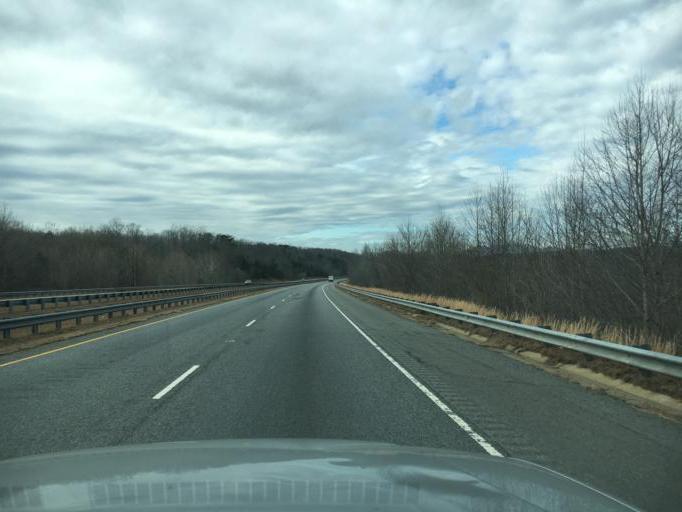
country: US
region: North Carolina
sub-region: Rutherford County
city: Rutherfordton
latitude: 35.2954
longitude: -81.9759
